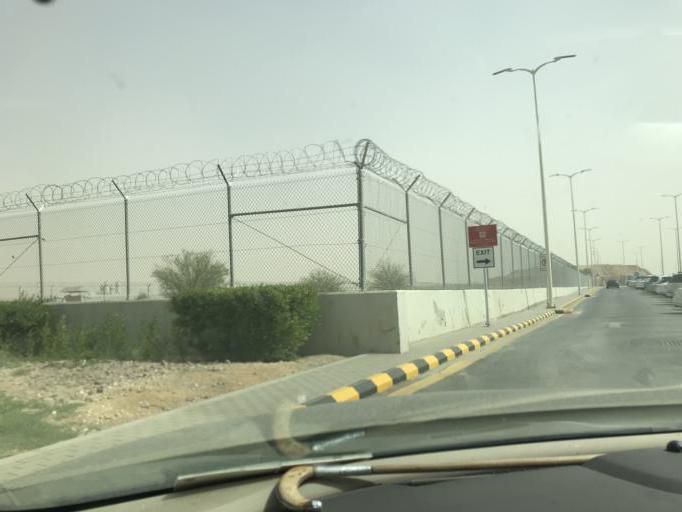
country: SA
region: Ar Riyad
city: Riyadh
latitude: 24.9399
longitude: 46.7130
